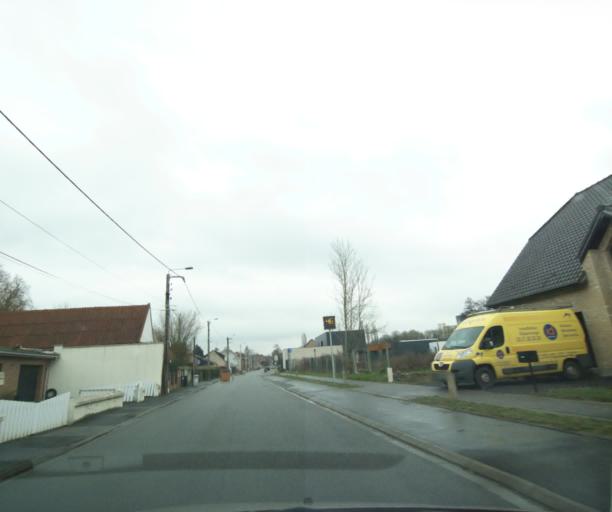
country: FR
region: Nord-Pas-de-Calais
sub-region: Departement du Nord
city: Haulchin
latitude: 50.3227
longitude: 3.4431
